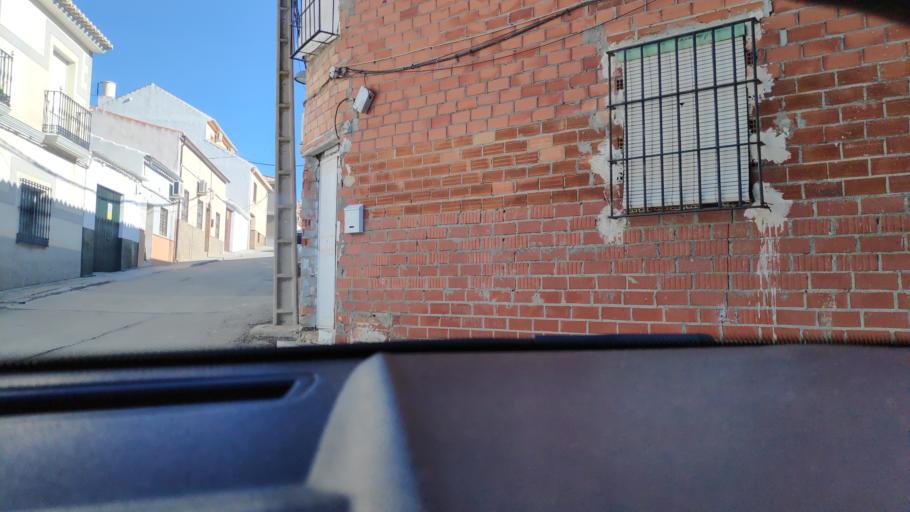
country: ES
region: Andalusia
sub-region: Province of Cordoba
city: Baena
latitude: 37.6144
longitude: -4.3348
